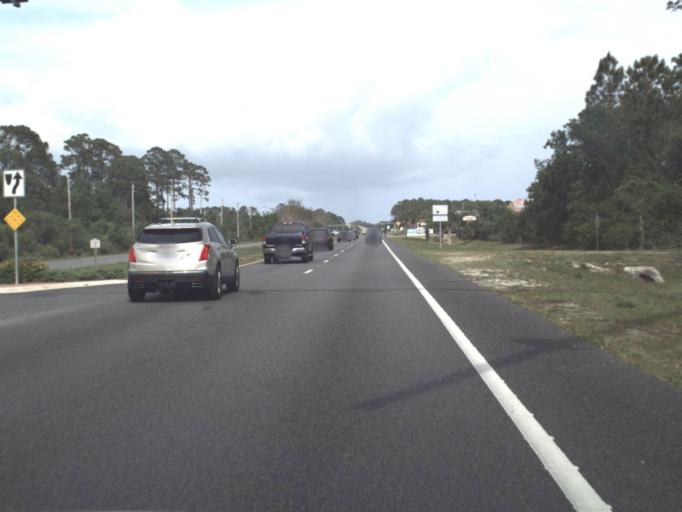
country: US
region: Florida
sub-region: Flagler County
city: Flagler Beach
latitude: 29.4765
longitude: -81.1537
